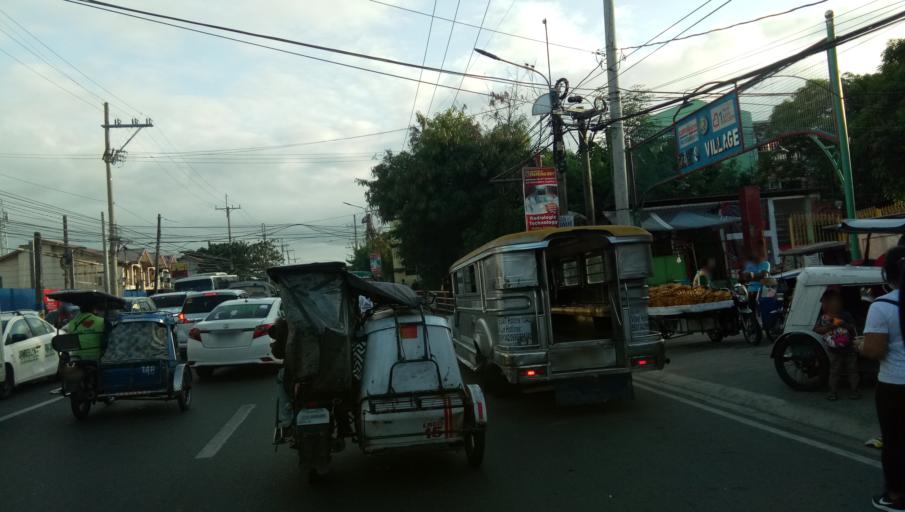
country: PH
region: Calabarzon
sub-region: Province of Cavite
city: Imus
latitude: 14.3828
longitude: 120.9783
